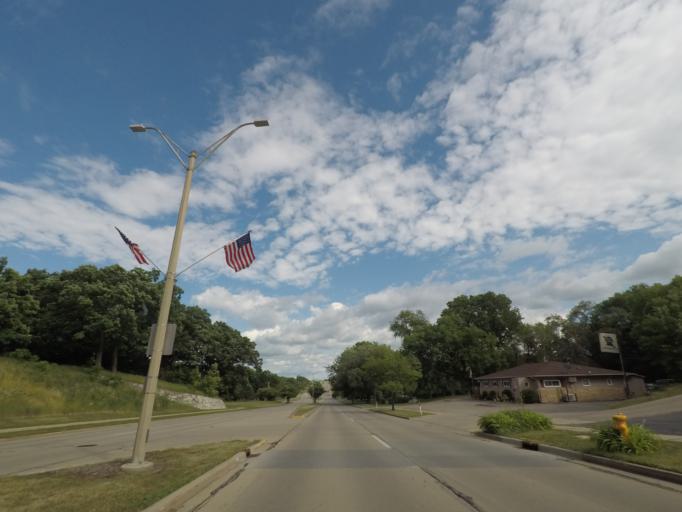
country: US
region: Wisconsin
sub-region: Rock County
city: Janesville
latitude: 42.6776
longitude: -88.9972
